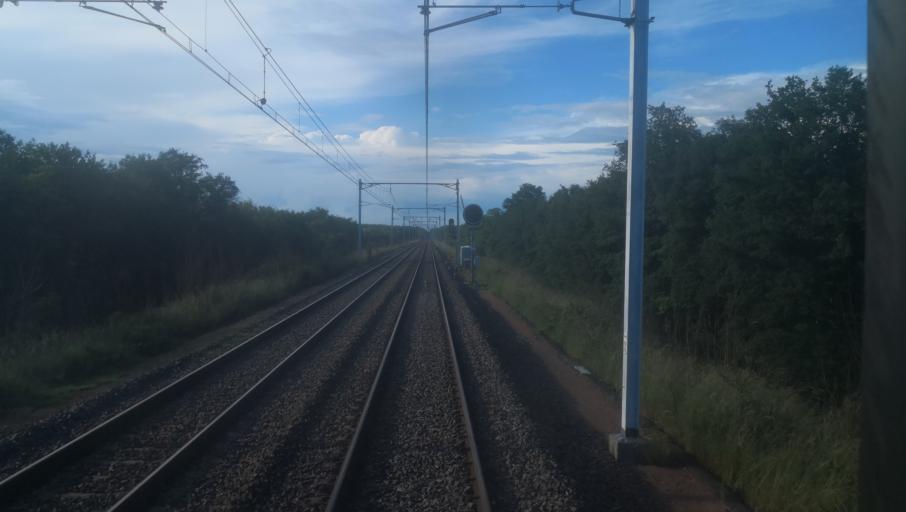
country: FR
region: Centre
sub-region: Departement du Loir-et-Cher
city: Theillay
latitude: 47.3310
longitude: 2.0458
